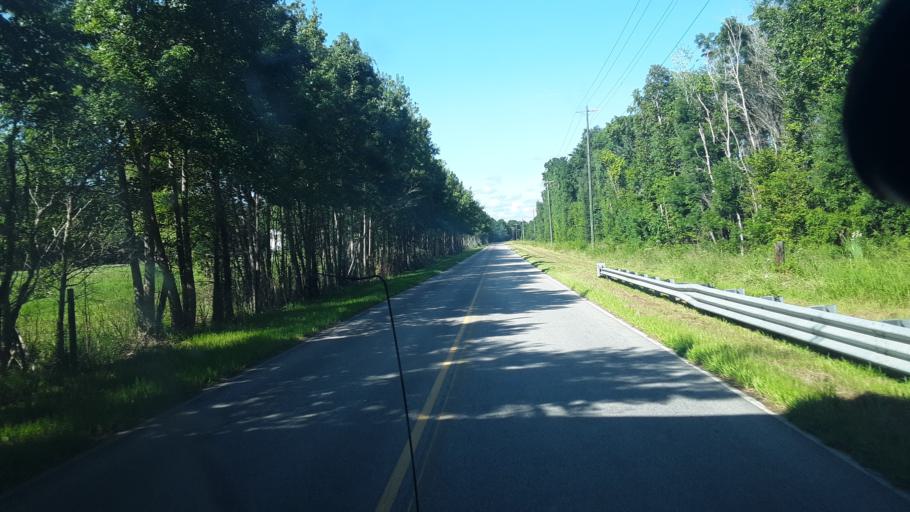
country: US
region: South Carolina
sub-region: Hampton County
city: Yemassee
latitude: 32.5954
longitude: -80.9133
